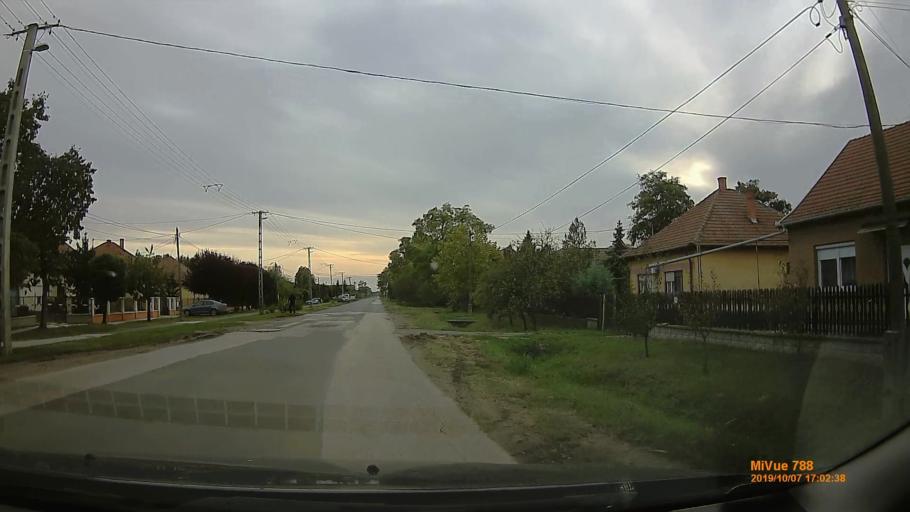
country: HU
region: Bekes
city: Szarvas
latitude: 46.8512
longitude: 20.5570
